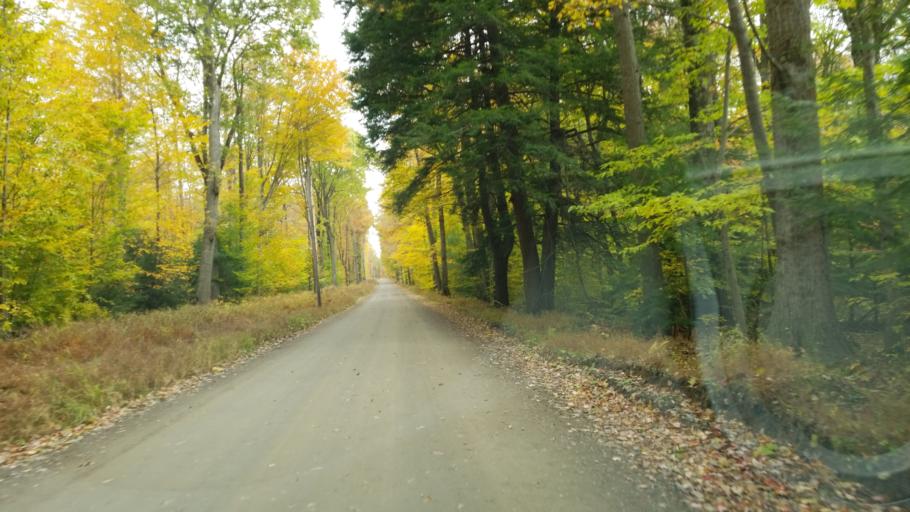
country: US
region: Pennsylvania
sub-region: Clearfield County
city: Shiloh
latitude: 41.1895
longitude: -78.3722
